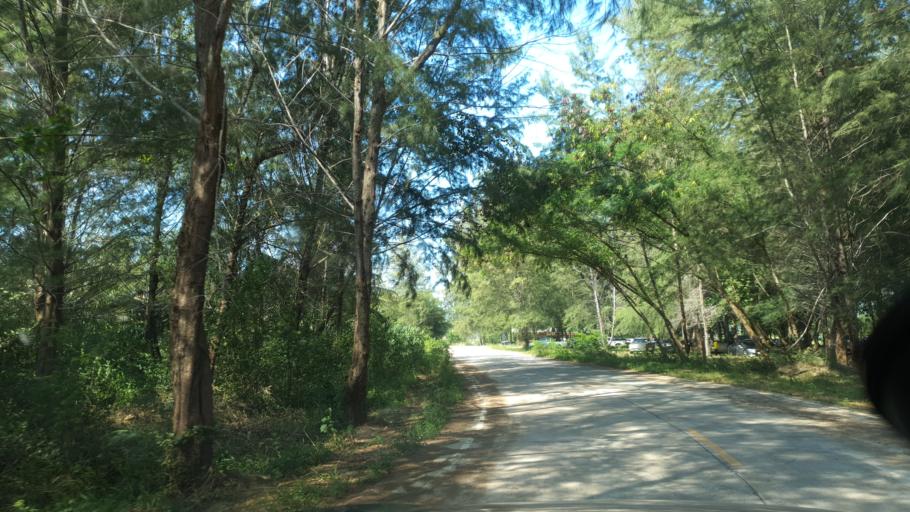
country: TH
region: Surat Thani
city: Tha Chana
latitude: 9.5984
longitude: 99.2096
